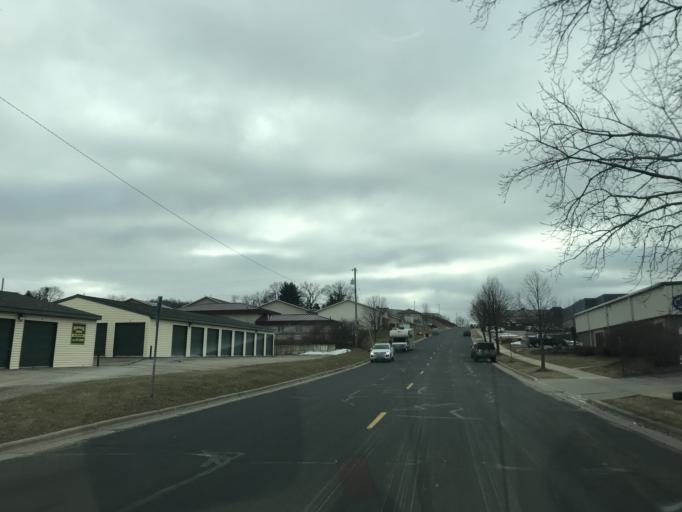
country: US
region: Wisconsin
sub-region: Dane County
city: Monona
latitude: 43.1100
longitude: -89.3101
